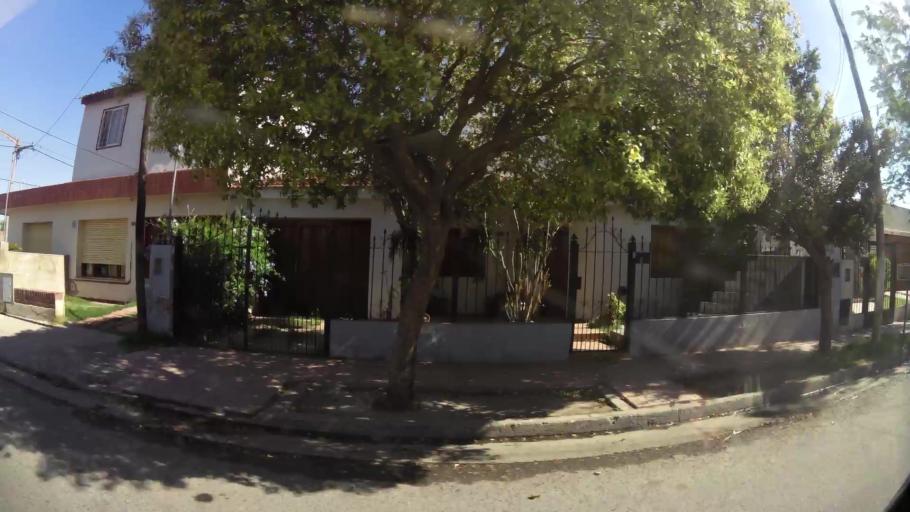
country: AR
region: Cordoba
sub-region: Departamento de Capital
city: Cordoba
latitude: -31.3608
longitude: -64.1704
